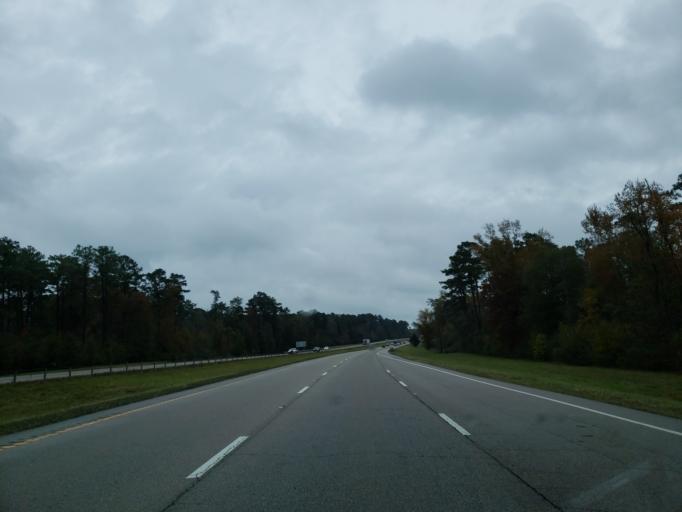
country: US
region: Mississippi
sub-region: Jones County
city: Ellisville
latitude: 31.5881
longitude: -89.2367
